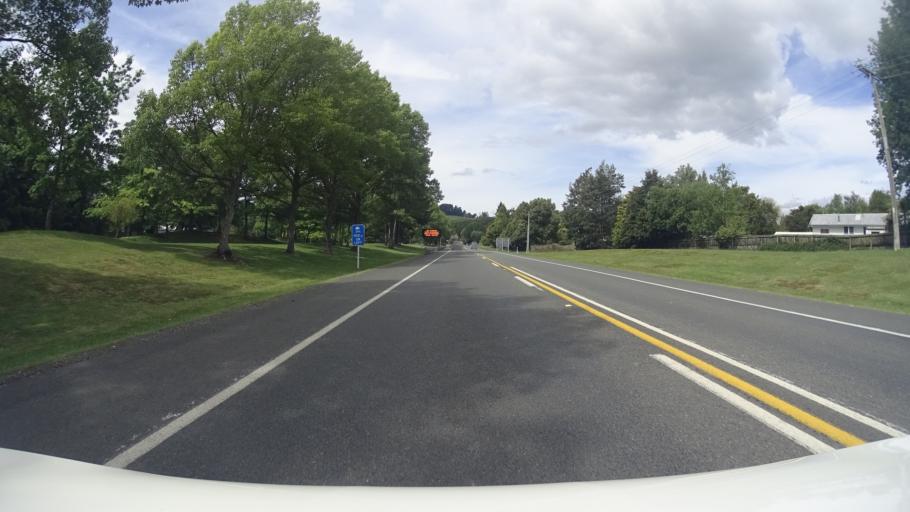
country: NZ
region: Waikato
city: Turangi
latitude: -38.9897
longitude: 175.8128
